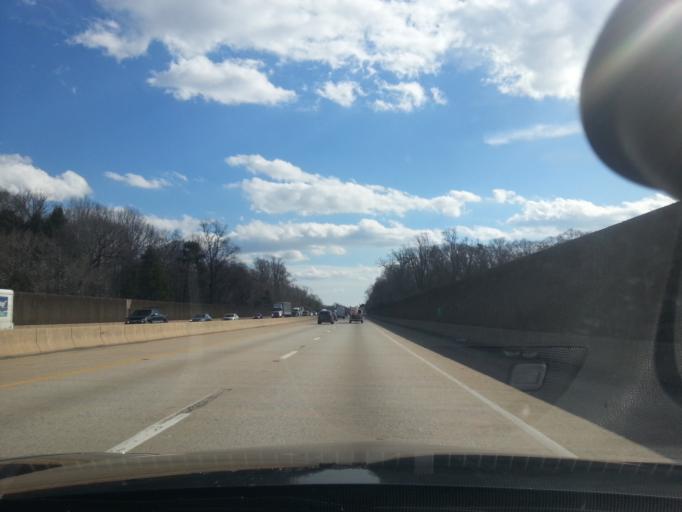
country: US
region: Pennsylvania
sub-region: Delaware County
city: Swarthmore
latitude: 39.9217
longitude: -75.3625
